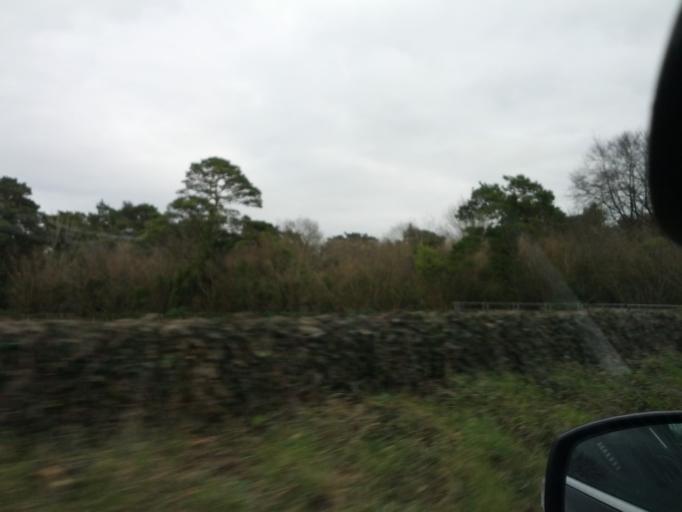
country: IE
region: Connaught
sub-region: County Galway
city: Athenry
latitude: 53.2663
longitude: -8.7427
